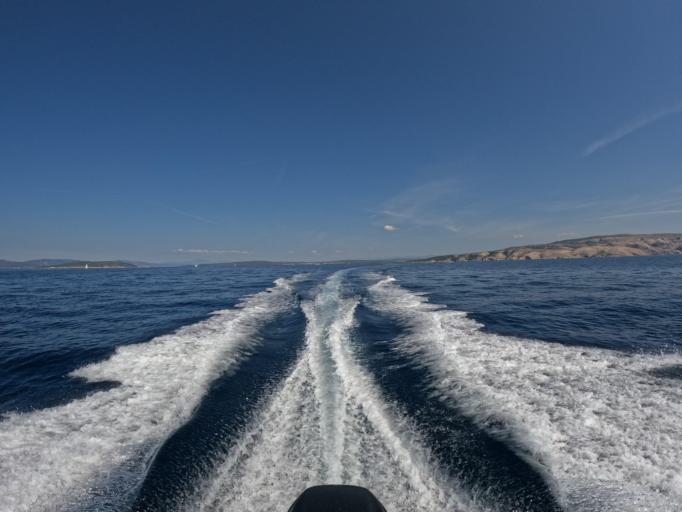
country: HR
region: Primorsko-Goranska
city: Punat
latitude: 44.9316
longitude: 14.6171
